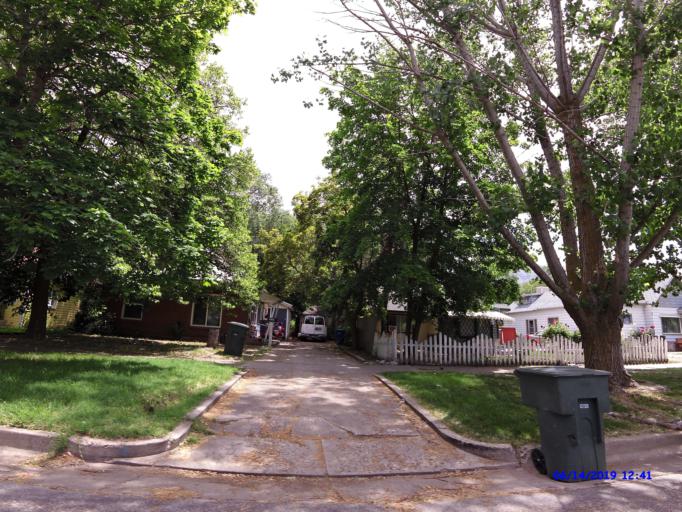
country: US
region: Utah
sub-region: Weber County
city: Ogden
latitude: 41.2259
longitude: -111.9536
